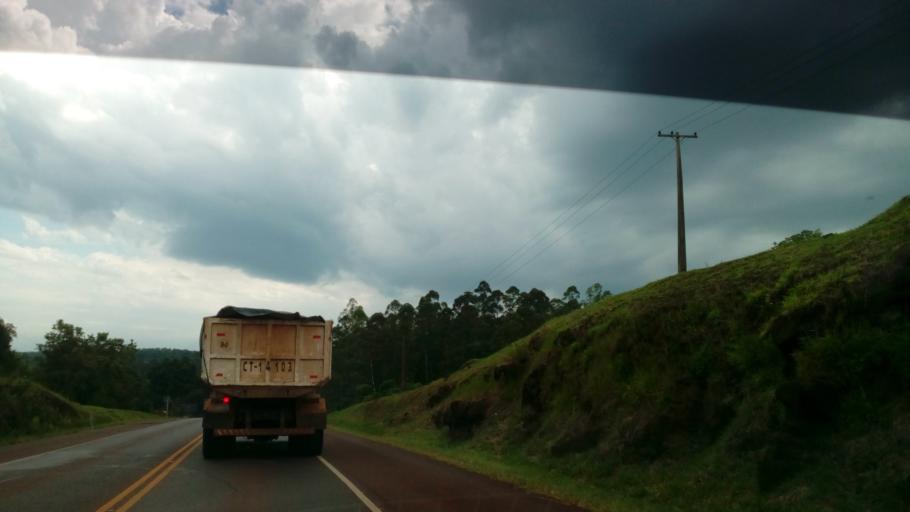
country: PY
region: Itapua
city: Obligado
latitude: -27.0651
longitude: -55.6047
